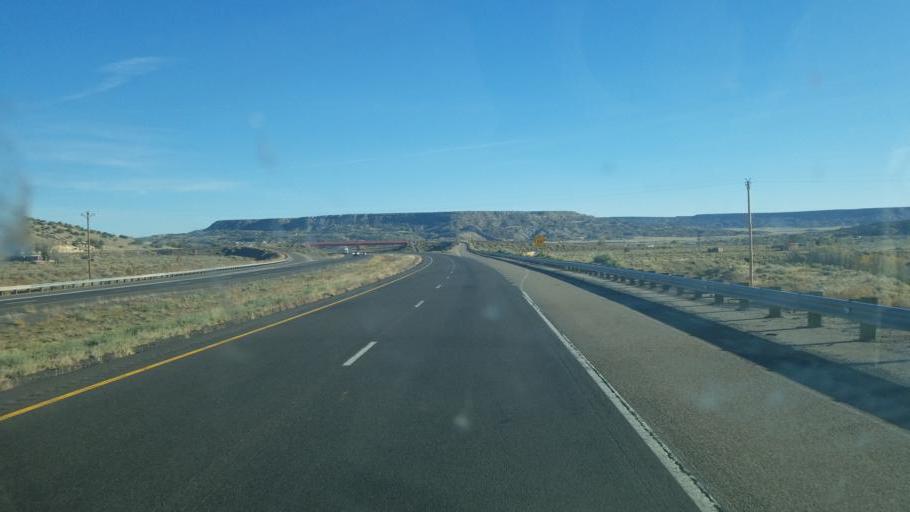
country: US
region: New Mexico
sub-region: Cibola County
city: Skyline-Ganipa
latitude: 35.0591
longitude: -107.5258
